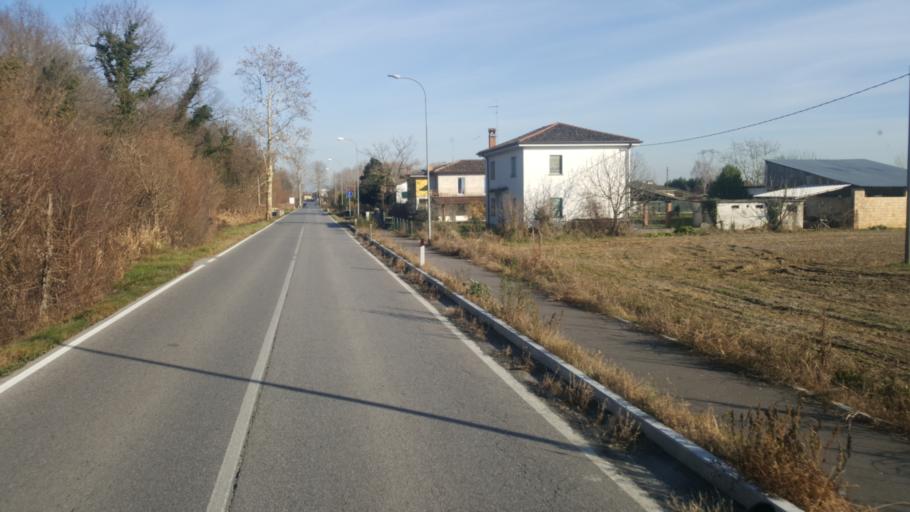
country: IT
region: Friuli Venezia Giulia
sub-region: Provincia di Udine
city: Carlino
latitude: 45.8286
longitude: 13.1675
